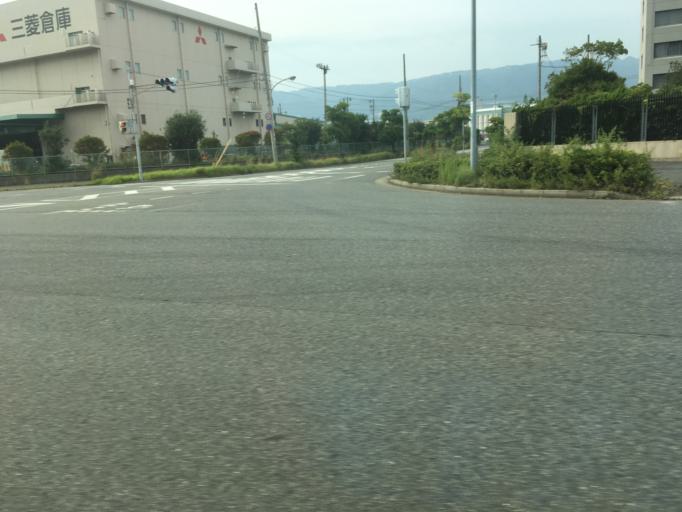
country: JP
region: Hyogo
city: Ashiya
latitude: 34.6935
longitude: 135.2650
